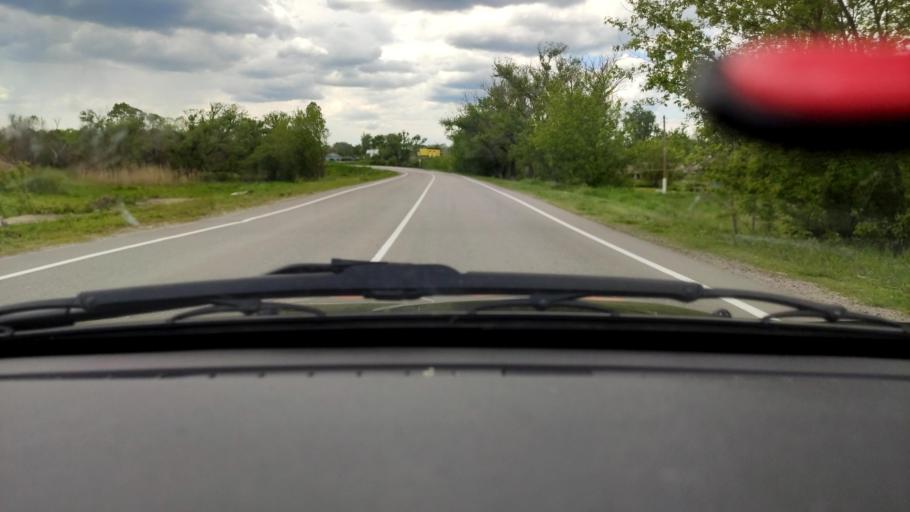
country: RU
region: Voronezj
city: Ostrogozhsk
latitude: 51.0552
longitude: 38.9232
